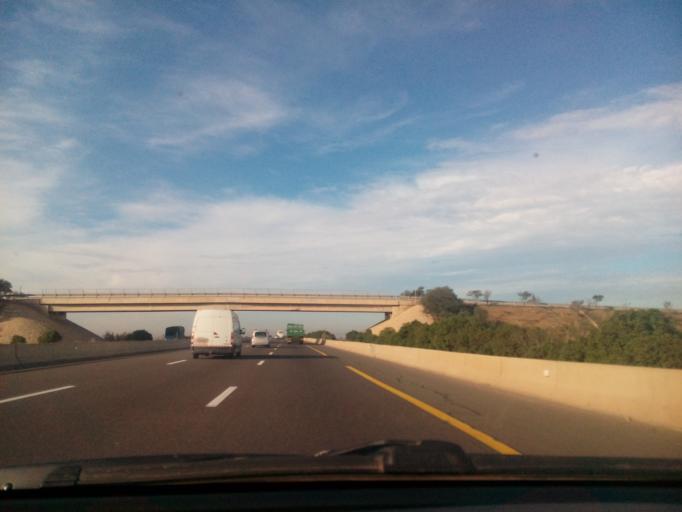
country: DZ
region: Mascara
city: Sig
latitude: 35.5874
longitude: -0.1163
